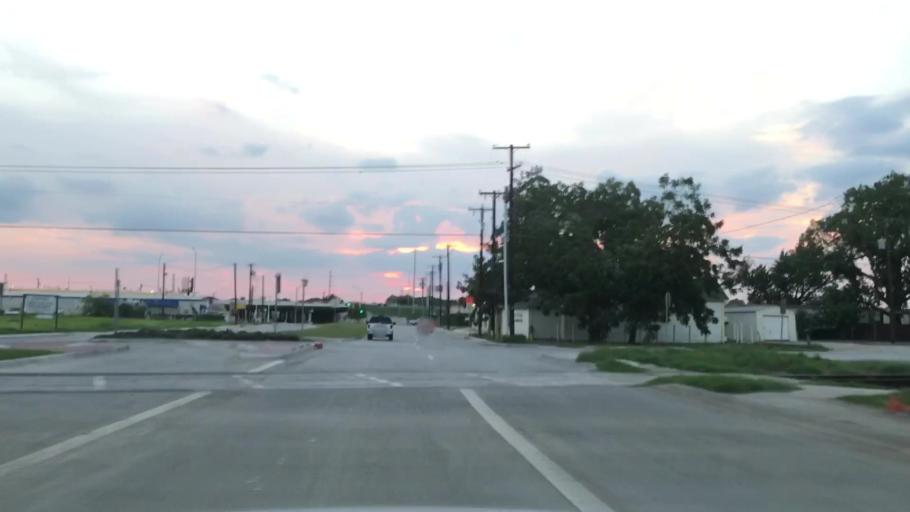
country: US
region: Texas
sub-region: Dallas County
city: Carrollton
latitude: 32.9686
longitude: -96.9166
